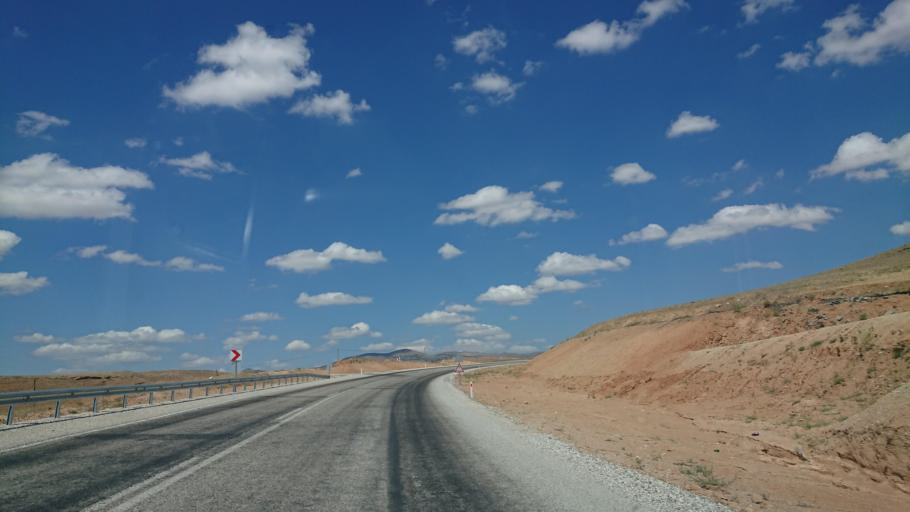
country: TR
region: Ankara
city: Evren
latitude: 39.1052
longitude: 33.9119
